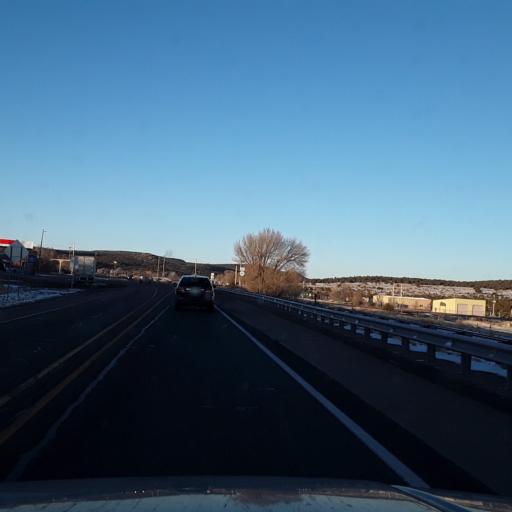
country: US
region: New Mexico
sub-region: Lincoln County
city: Carrizozo
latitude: 34.2431
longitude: -105.5958
